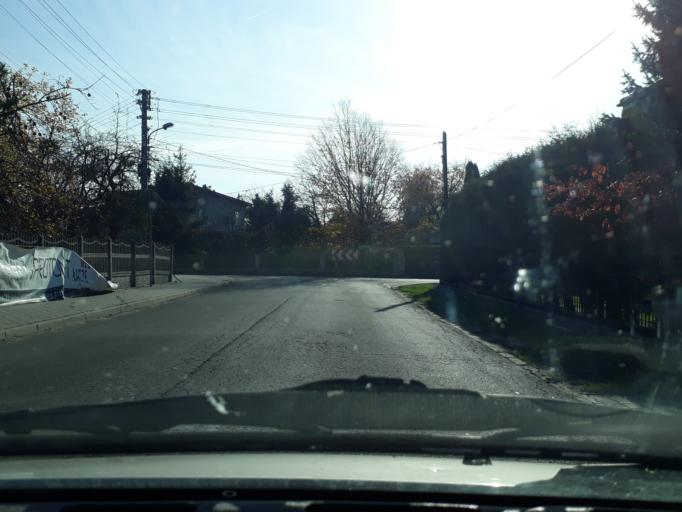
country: PL
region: Silesian Voivodeship
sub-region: Powiat tarnogorski
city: Tarnowskie Gory
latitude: 50.4285
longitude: 18.8440
